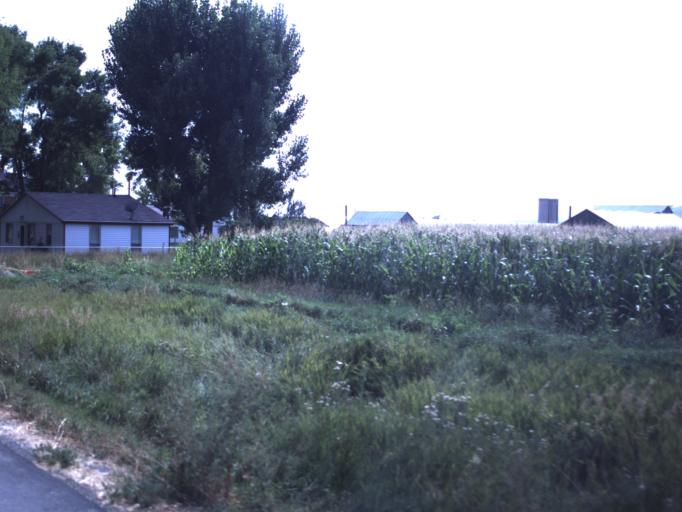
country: US
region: Utah
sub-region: Box Elder County
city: Garland
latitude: 41.7985
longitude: -112.1158
